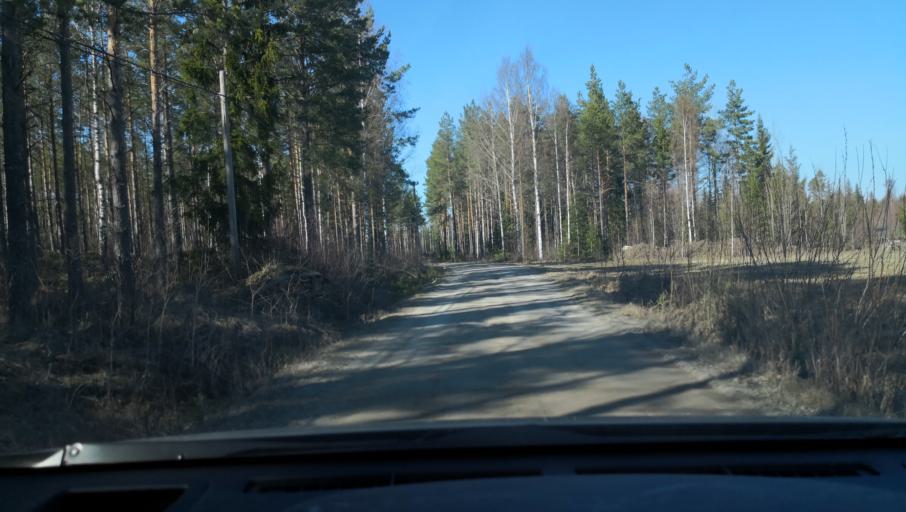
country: SE
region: Vaestmanland
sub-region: Sala Kommun
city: Sala
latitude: 59.9326
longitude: 16.4504
